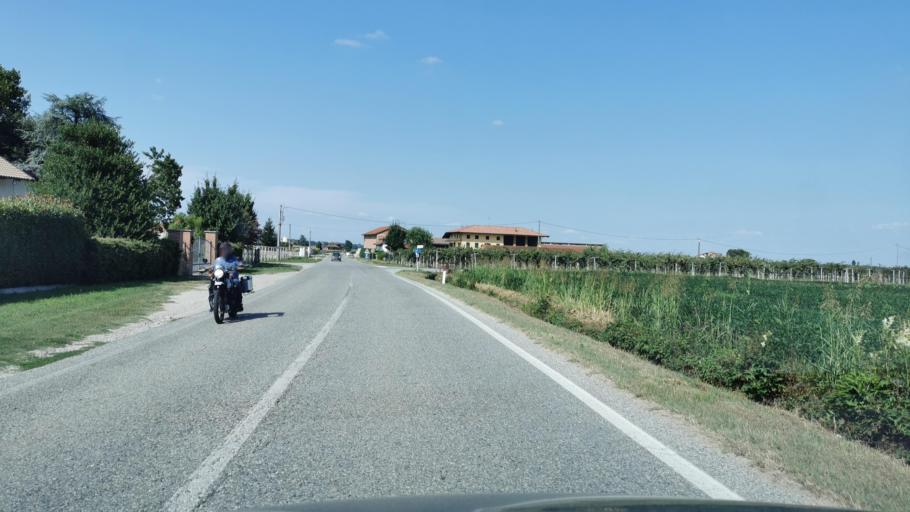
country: IT
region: Piedmont
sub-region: Provincia di Cuneo
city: Revello
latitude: 44.6791
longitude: 7.4106
